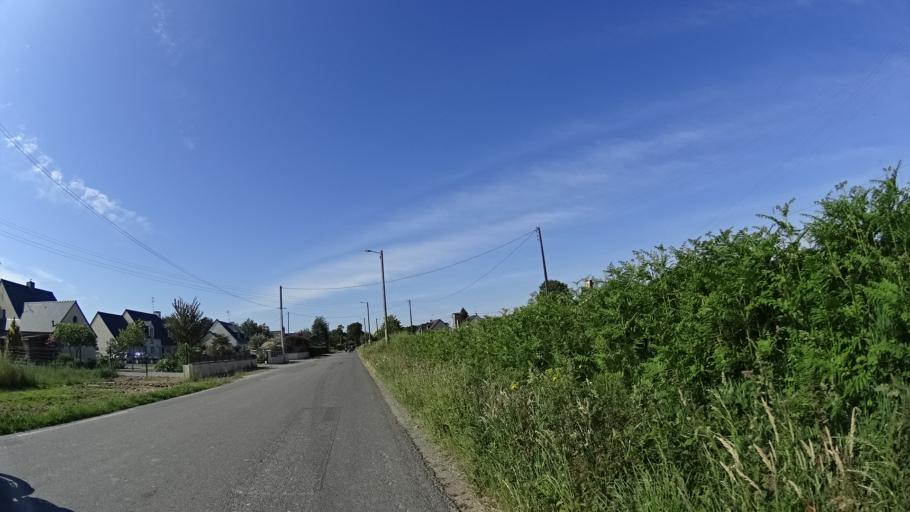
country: FR
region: Brittany
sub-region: Departement d'Ille-et-Vilaine
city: Guipry
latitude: 47.8170
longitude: -1.8483
